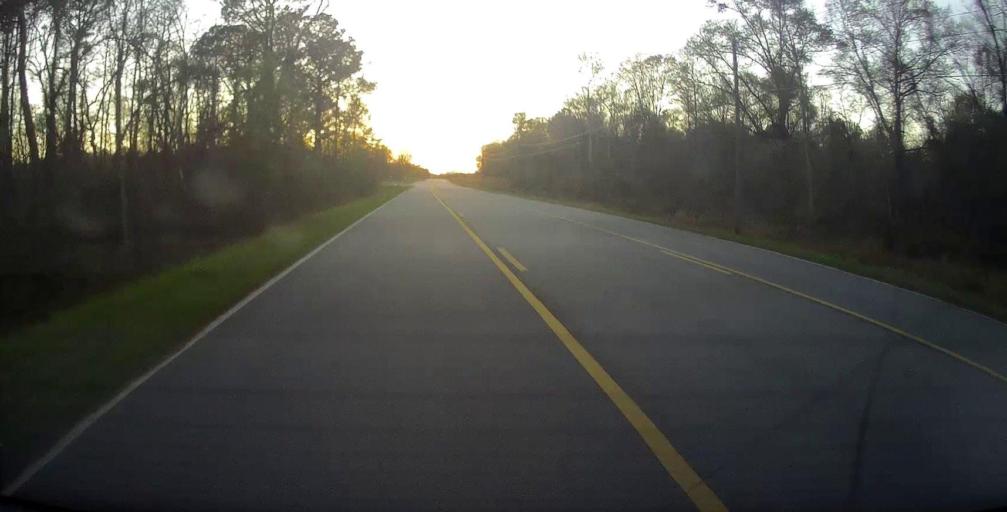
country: US
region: Georgia
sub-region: Crisp County
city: Cordele
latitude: 31.9259
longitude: -83.7535
